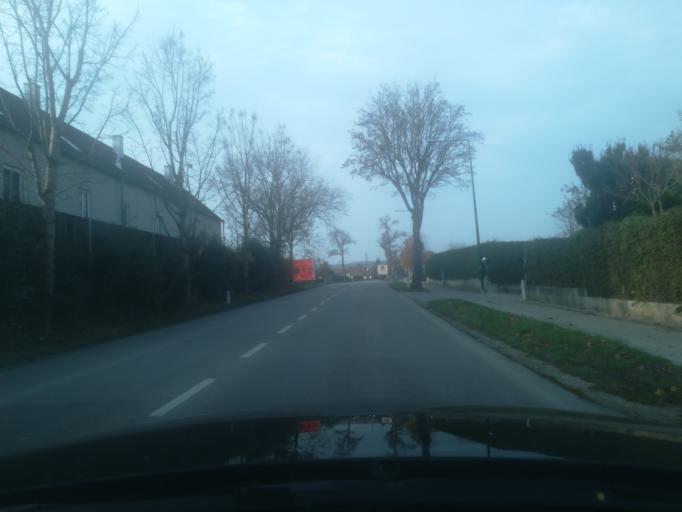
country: AT
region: Upper Austria
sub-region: Wels Stadt
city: Wels
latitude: 48.1688
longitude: 13.9975
